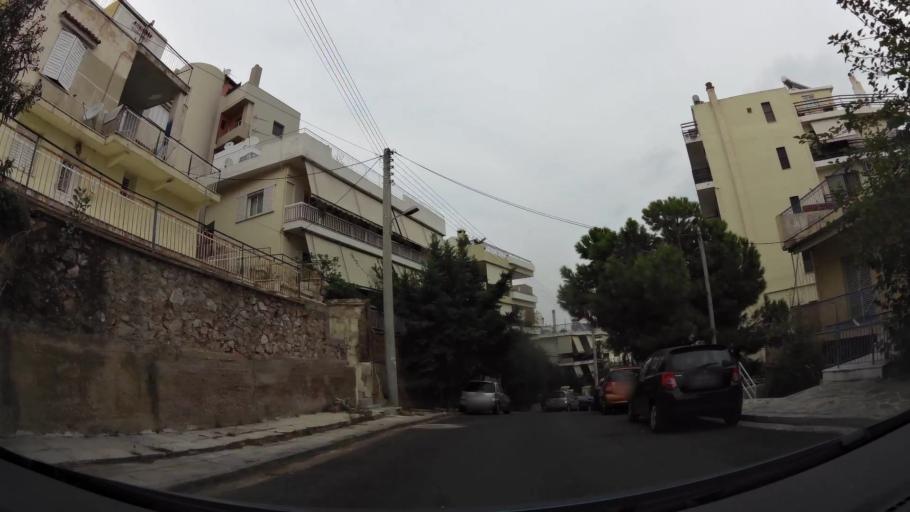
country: GR
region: Attica
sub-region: Nomarchia Athinas
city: Agios Dimitrios
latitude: 37.9259
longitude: 23.7364
